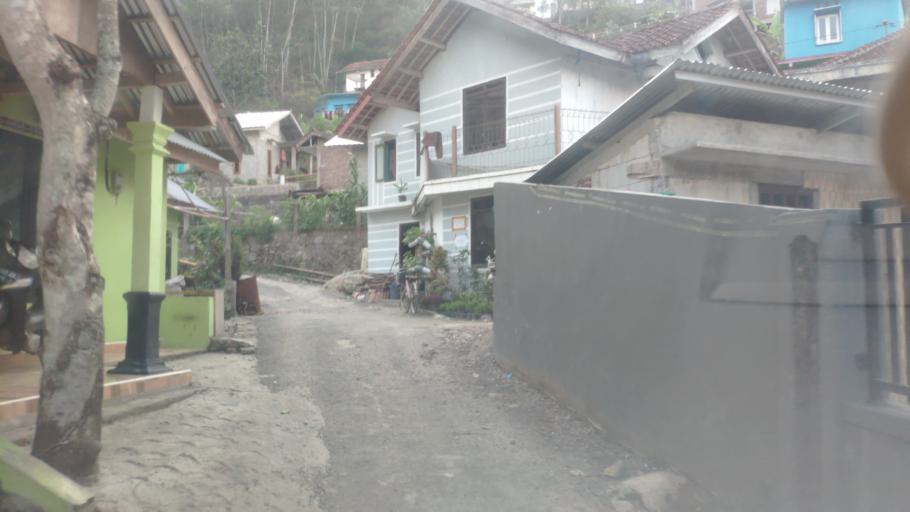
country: ID
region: Central Java
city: Buaran
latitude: -7.2451
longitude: 109.5842
